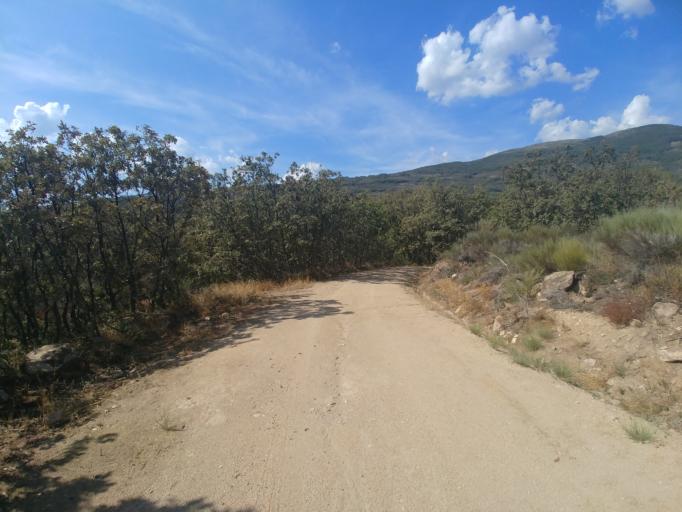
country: ES
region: Extremadura
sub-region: Provincia de Caceres
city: Garganta la Olla
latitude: 40.1015
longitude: -5.7383
